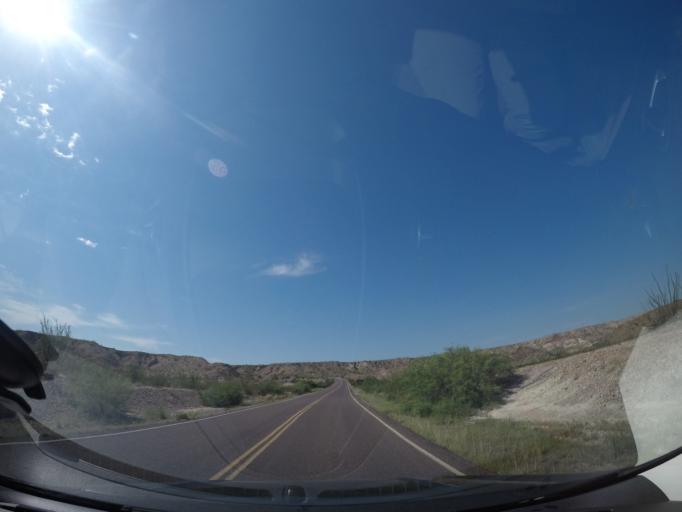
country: US
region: Texas
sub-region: Presidio County
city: Presidio
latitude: 29.2971
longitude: -103.5033
